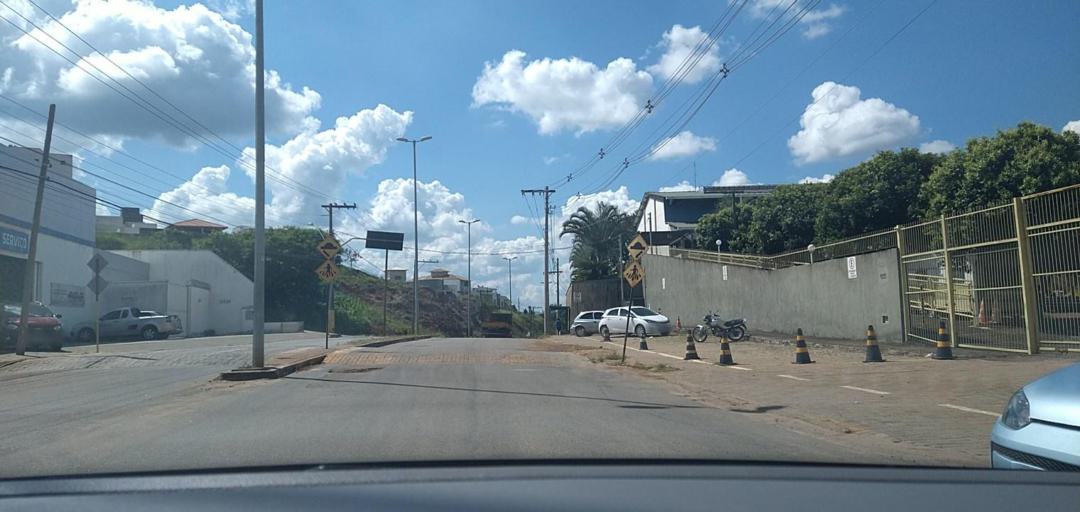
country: BR
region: Minas Gerais
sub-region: Joao Monlevade
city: Joao Monlevade
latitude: -19.8281
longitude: -43.1886
